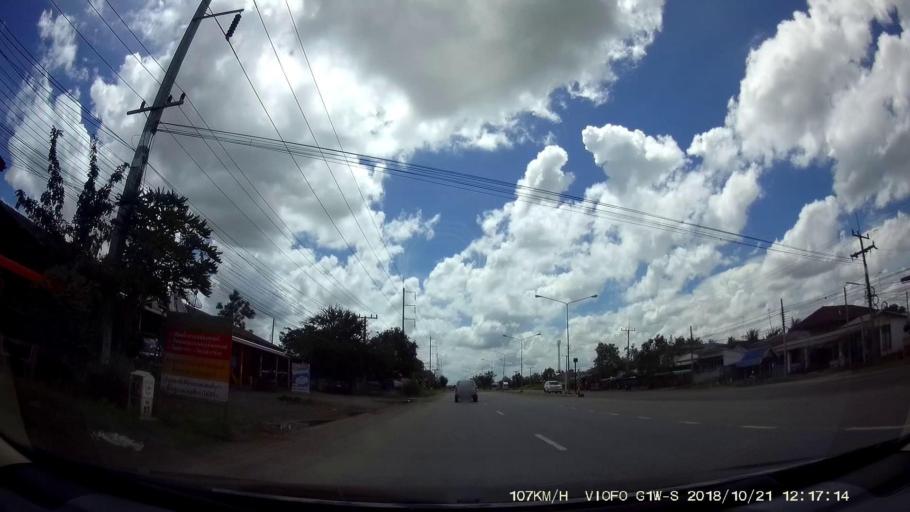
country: TH
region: Nakhon Ratchasima
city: Dan Khun Thot
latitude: 15.3351
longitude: 101.8215
